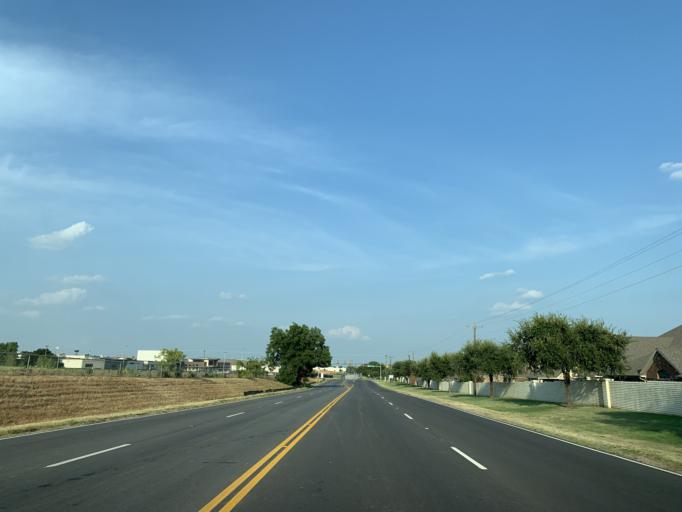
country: US
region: Texas
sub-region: Tarrant County
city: Hurst
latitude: 32.8021
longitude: -97.1717
